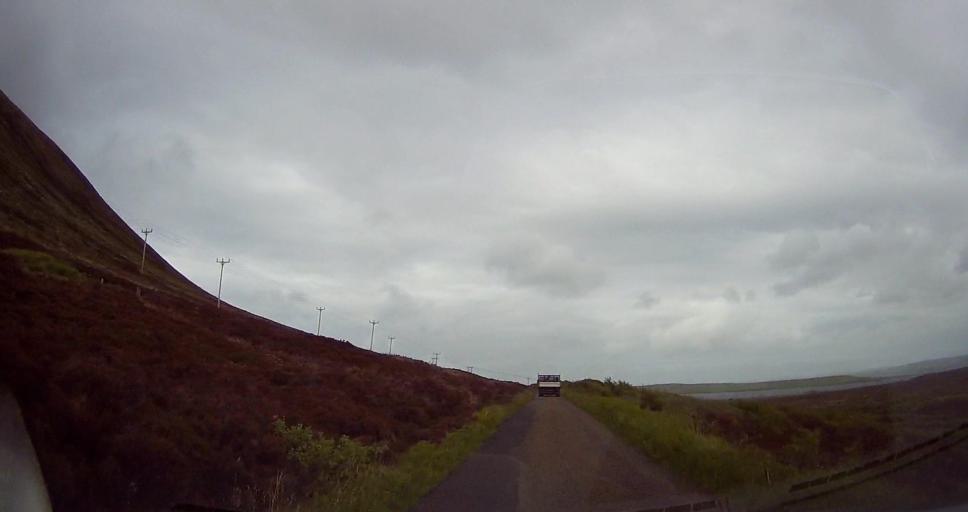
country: GB
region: Scotland
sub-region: Orkney Islands
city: Stromness
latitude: 58.8936
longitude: -3.3144
